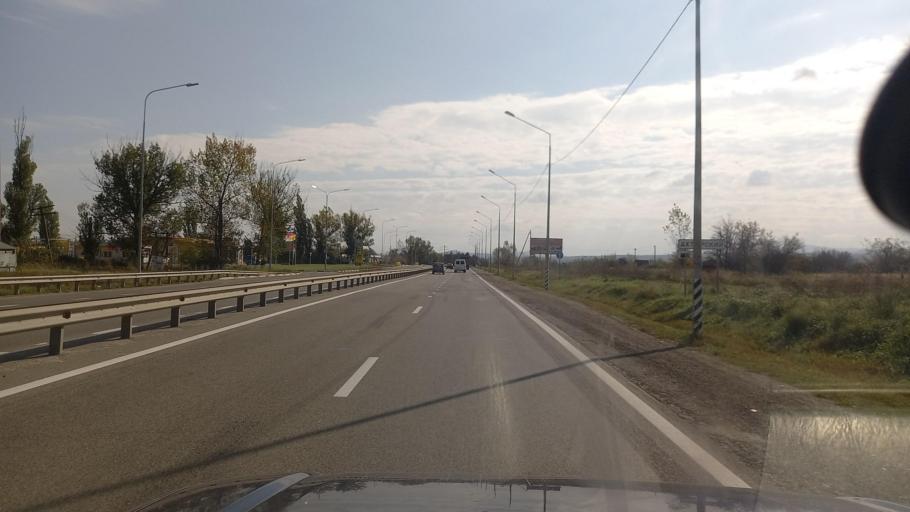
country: RU
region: Krasnodarskiy
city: Akhtyrskiy
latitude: 44.8490
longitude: 38.2756
